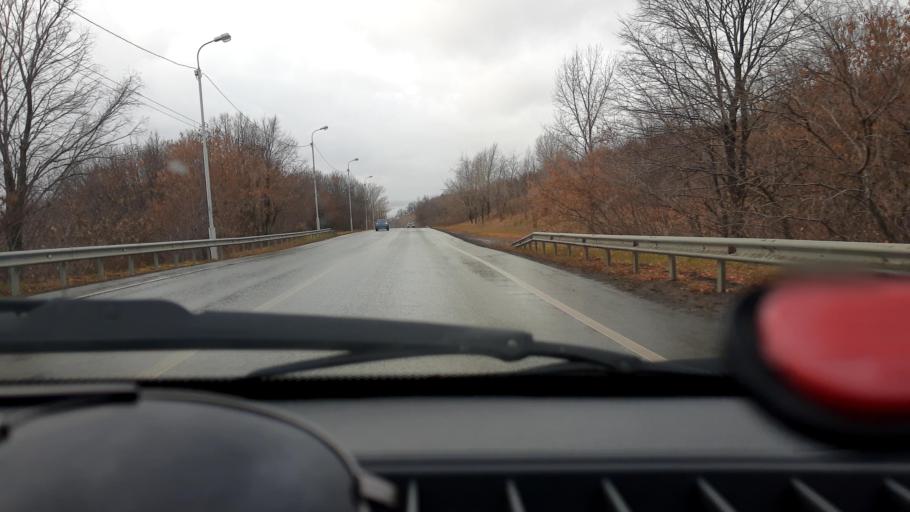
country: RU
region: Bashkortostan
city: Ufa
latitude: 54.8675
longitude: 56.0702
